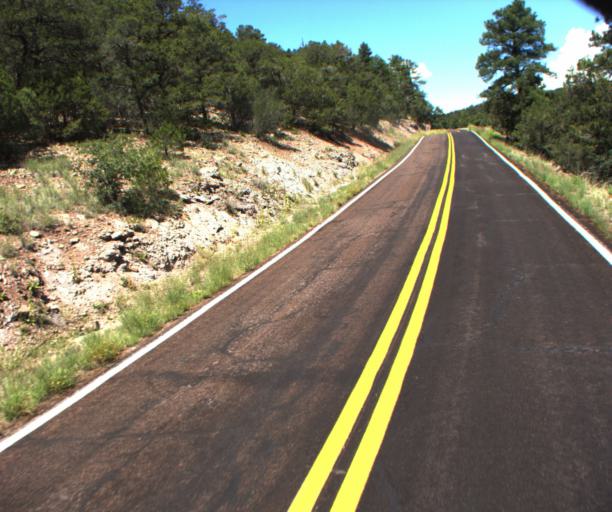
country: US
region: Arizona
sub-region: Greenlee County
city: Morenci
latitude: 33.3944
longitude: -109.3297
